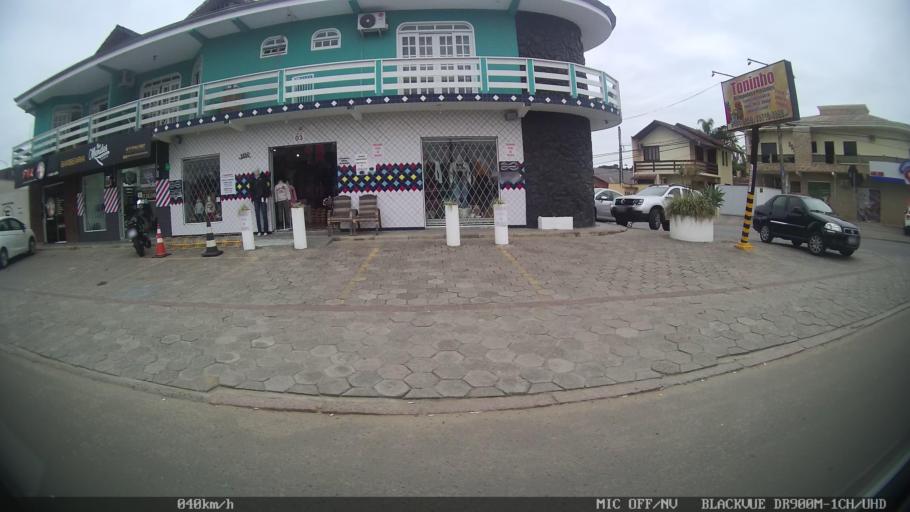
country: BR
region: Santa Catarina
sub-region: Joinville
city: Joinville
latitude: -26.3409
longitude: -48.8204
